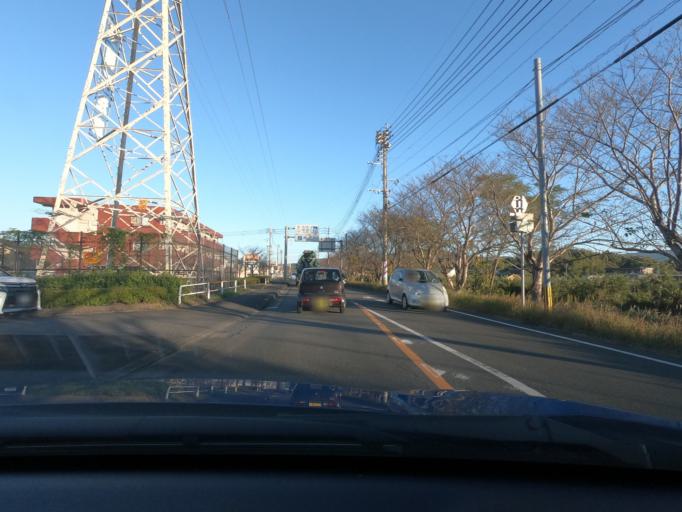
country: JP
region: Kagoshima
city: Satsumasendai
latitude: 31.8092
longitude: 130.3197
